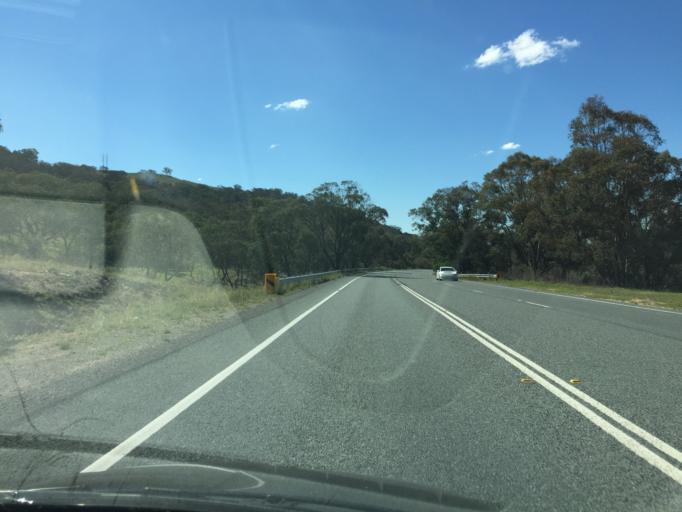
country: AU
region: Australian Capital Territory
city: Macarthur
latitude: -35.4714
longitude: 149.1388
